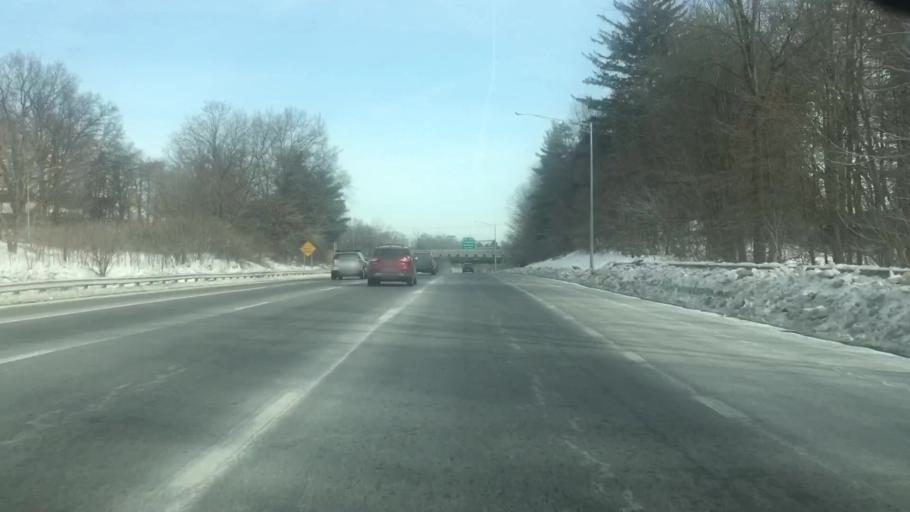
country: US
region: Connecticut
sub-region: Hartford County
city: West Hartford
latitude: 41.7485
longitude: -72.7319
